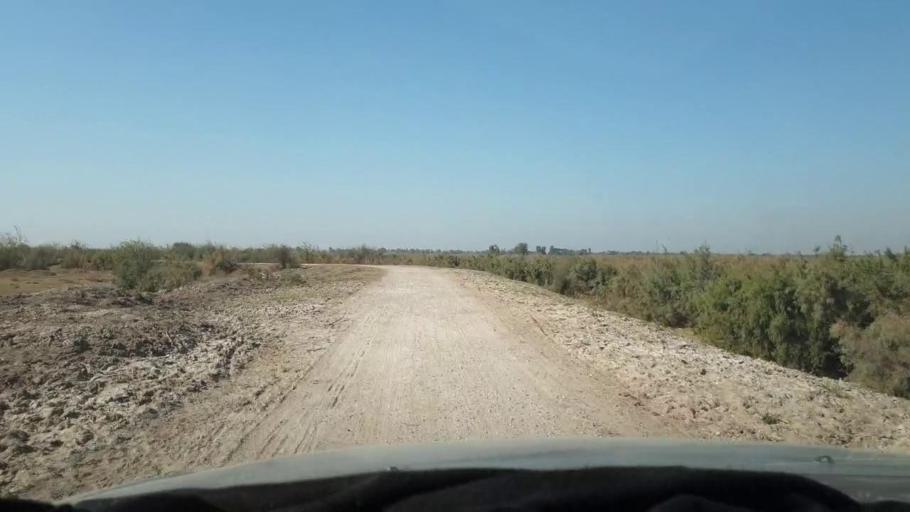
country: PK
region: Sindh
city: Adilpur
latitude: 27.8973
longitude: 69.2461
